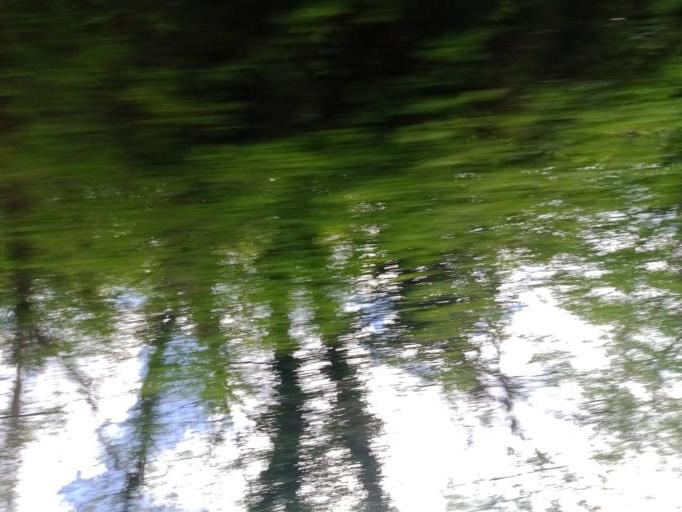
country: IE
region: Munster
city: Thurles
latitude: 52.6876
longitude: -7.6531
